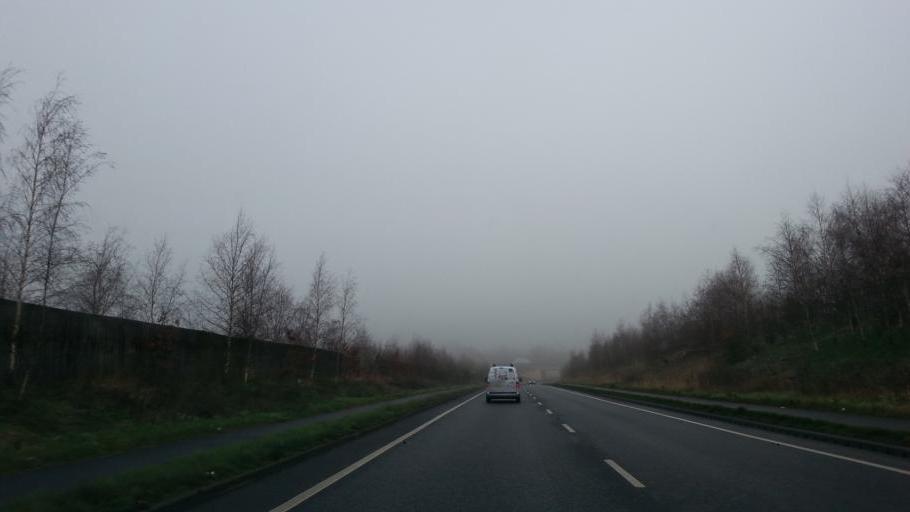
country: GB
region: England
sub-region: Cheshire East
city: Alderley Edge
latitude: 53.3041
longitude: -2.2472
